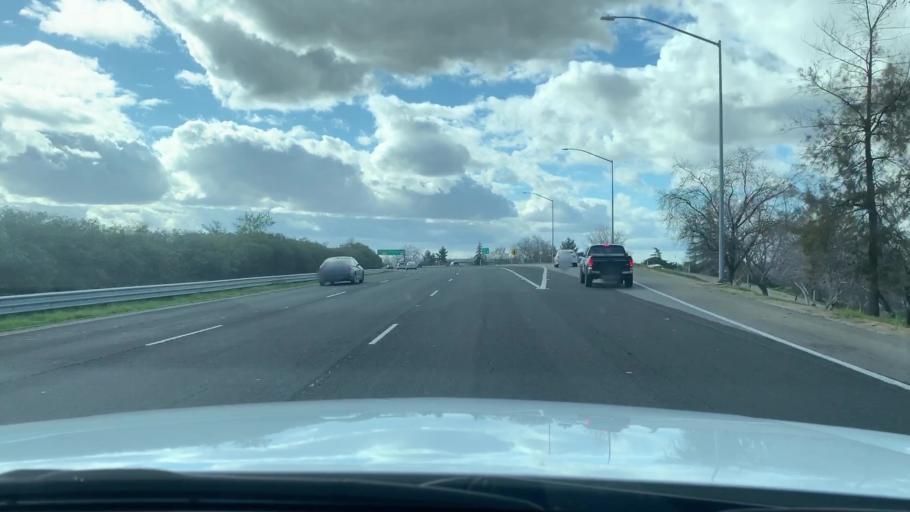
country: US
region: California
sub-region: Kern County
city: Bakersfield
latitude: 35.3837
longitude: -119.0045
